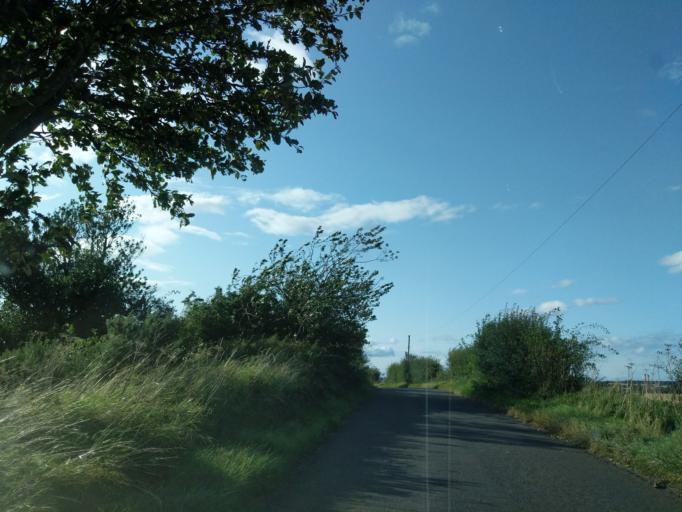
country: GB
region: Scotland
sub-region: East Lothian
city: Haddington
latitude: 56.0038
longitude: -2.7800
